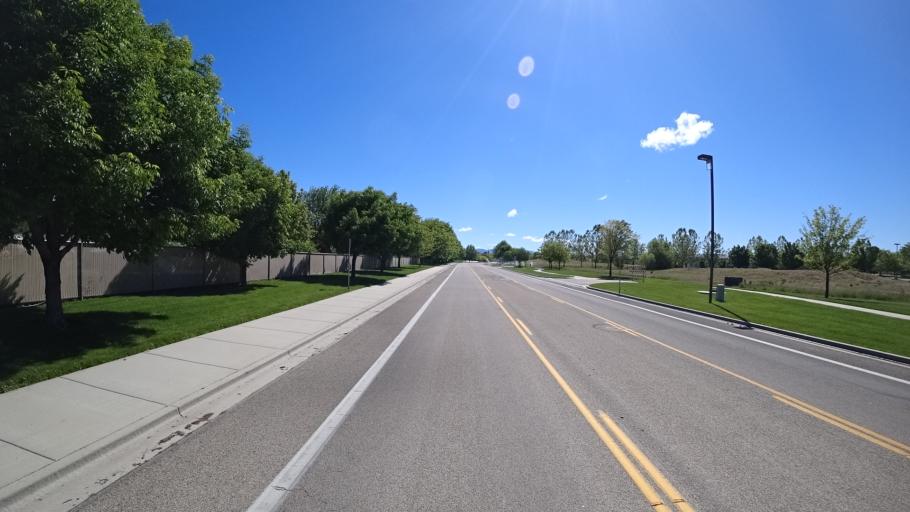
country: US
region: Idaho
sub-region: Ada County
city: Meridian
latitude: 43.6410
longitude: -116.3733
